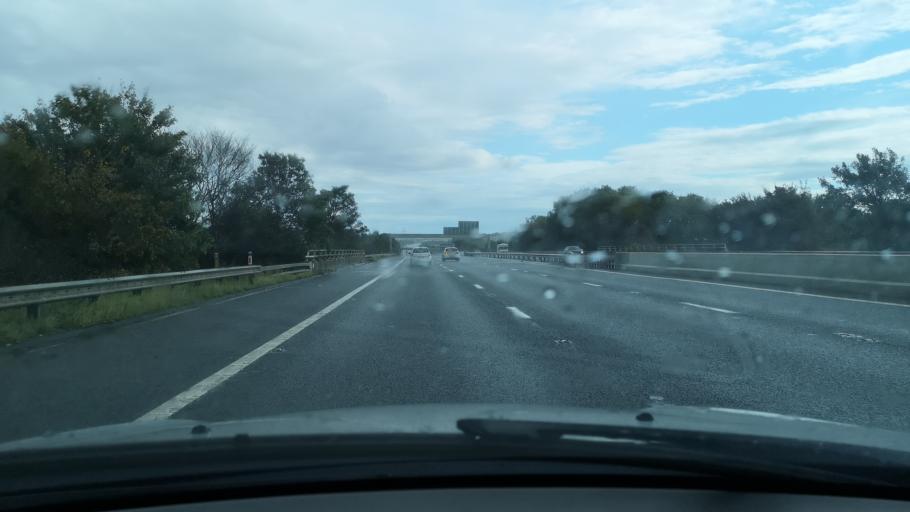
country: GB
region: England
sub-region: City and Borough of Wakefield
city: Knottingley
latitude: 53.6930
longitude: -1.2361
